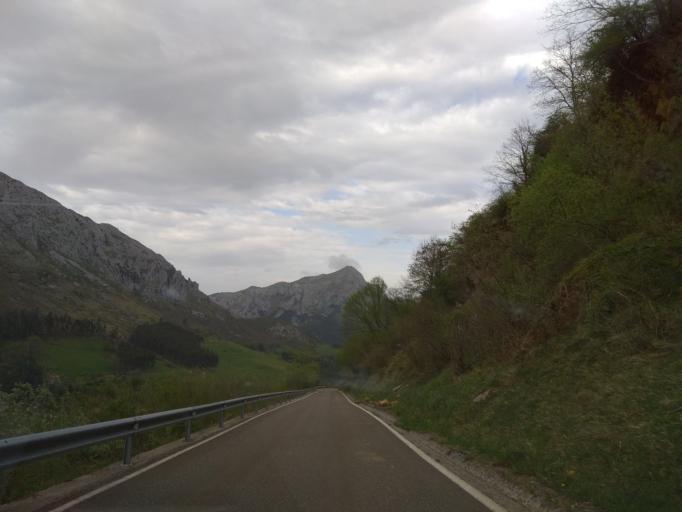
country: ES
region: Cantabria
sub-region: Provincia de Cantabria
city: Cabezon de Liebana
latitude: 43.2513
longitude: -4.5157
